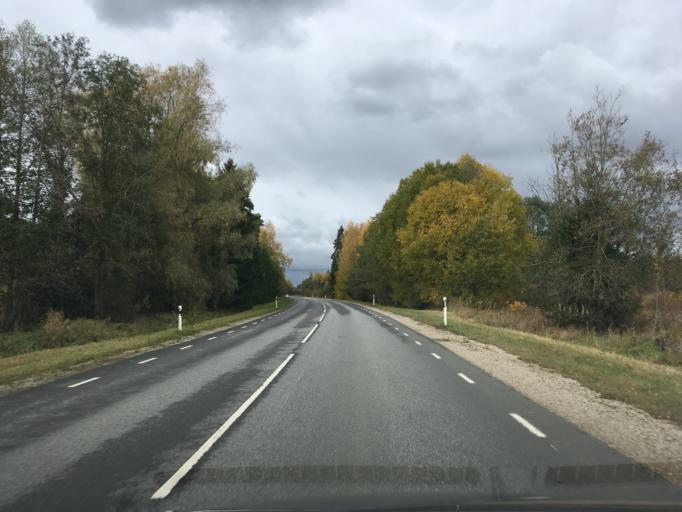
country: EE
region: Harju
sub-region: Anija vald
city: Kehra
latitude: 59.2947
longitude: 25.3734
